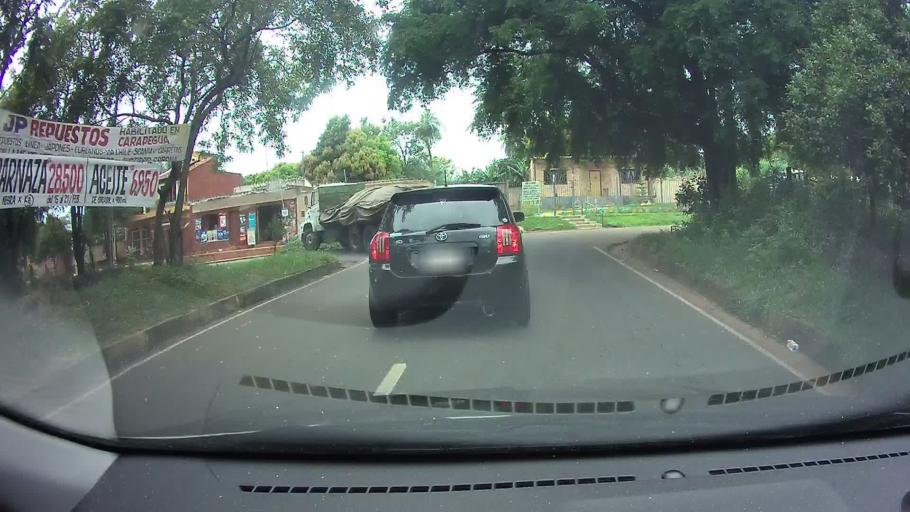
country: PY
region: Paraguari
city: Carapegua
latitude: -25.7615
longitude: -57.2513
